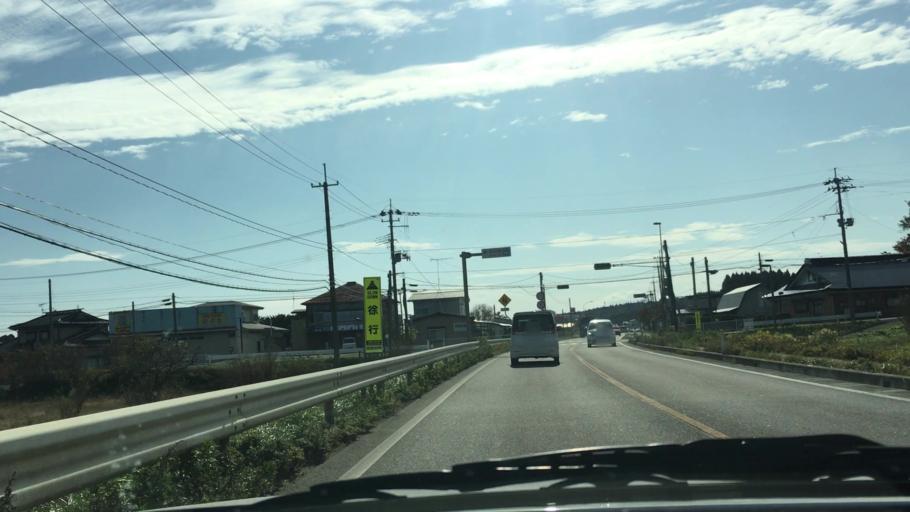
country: JP
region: Aomori
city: Hachinohe
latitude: 40.4237
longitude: 141.6982
